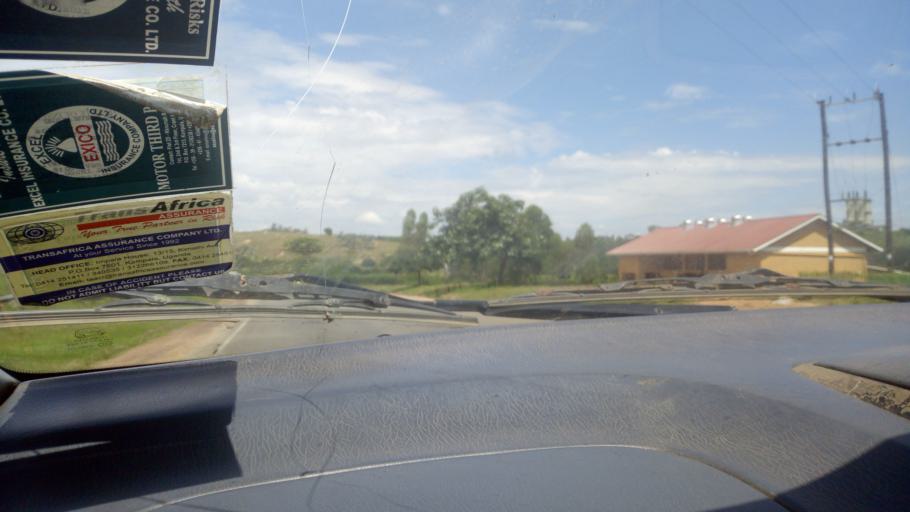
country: UG
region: Western Region
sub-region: Buhweju District
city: Buhweju
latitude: -0.2620
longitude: 30.5592
